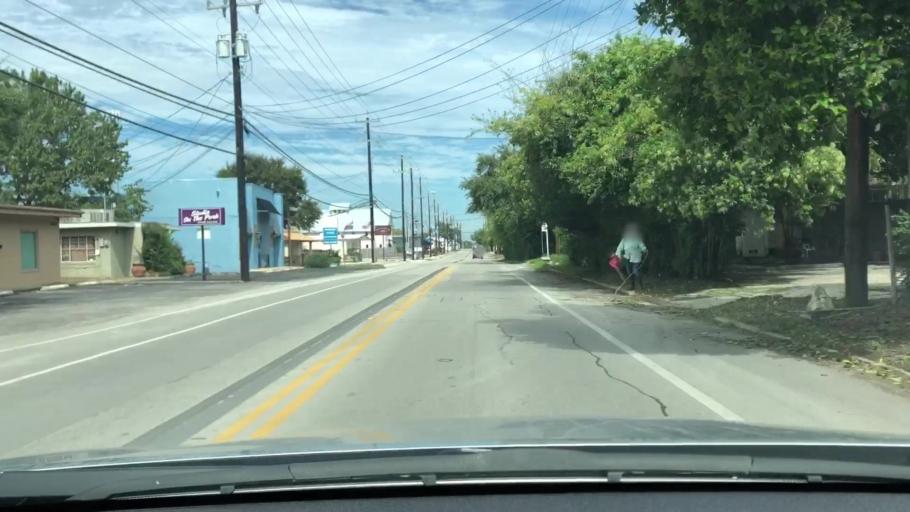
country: US
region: Texas
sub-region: Bexar County
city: Olmos Park
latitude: 29.4759
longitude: -98.4917
